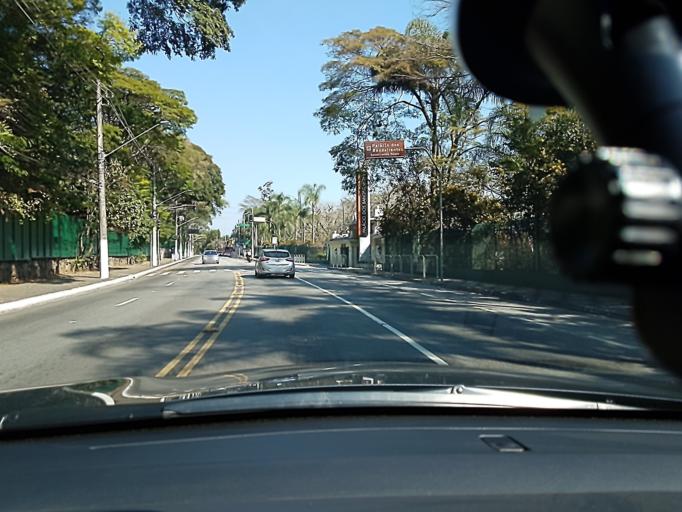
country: BR
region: Sao Paulo
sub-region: Taboao Da Serra
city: Taboao da Serra
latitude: -23.6024
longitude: -46.7119
